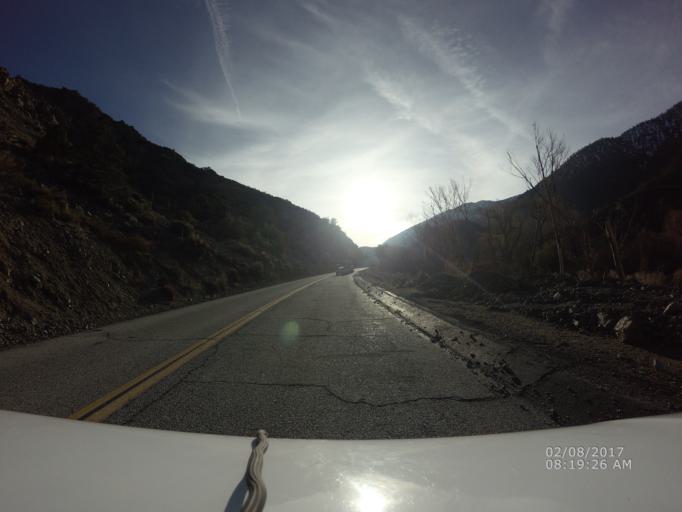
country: US
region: California
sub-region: San Bernardino County
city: Pinon Hills
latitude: 34.3976
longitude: -117.8035
